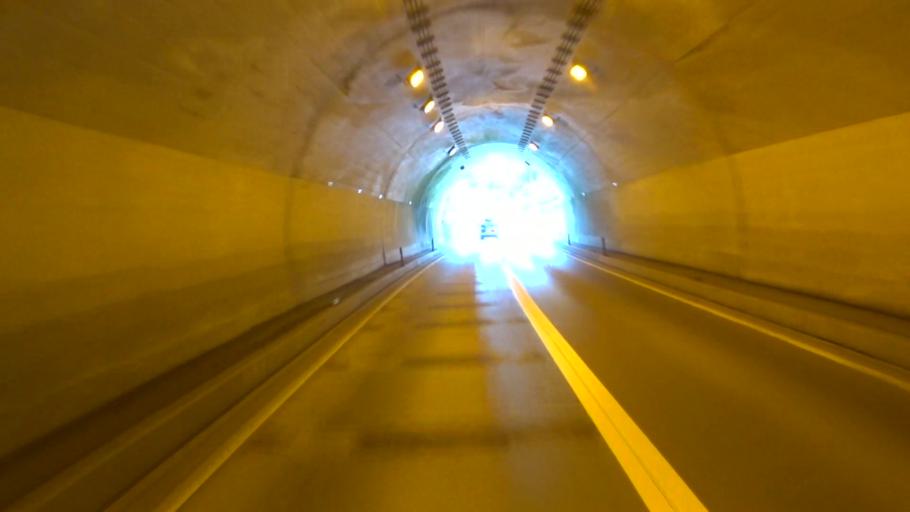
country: JP
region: Shiga Prefecture
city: Kitahama
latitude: 35.2056
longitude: 135.8574
